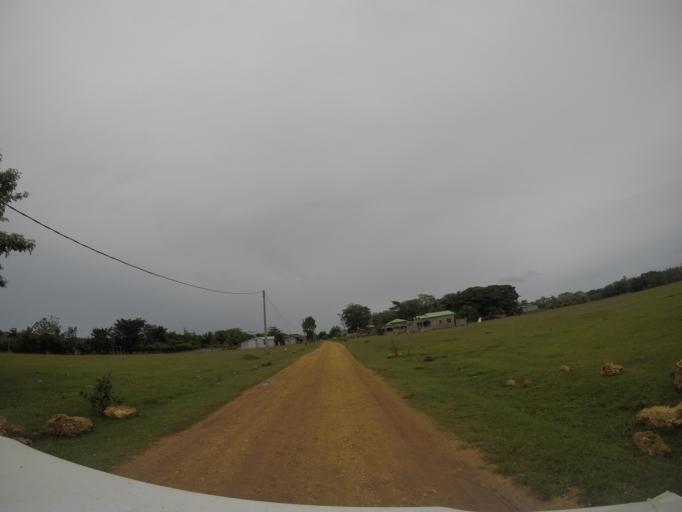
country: TL
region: Lautem
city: Lospalos
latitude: -8.5273
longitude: 127.0109
